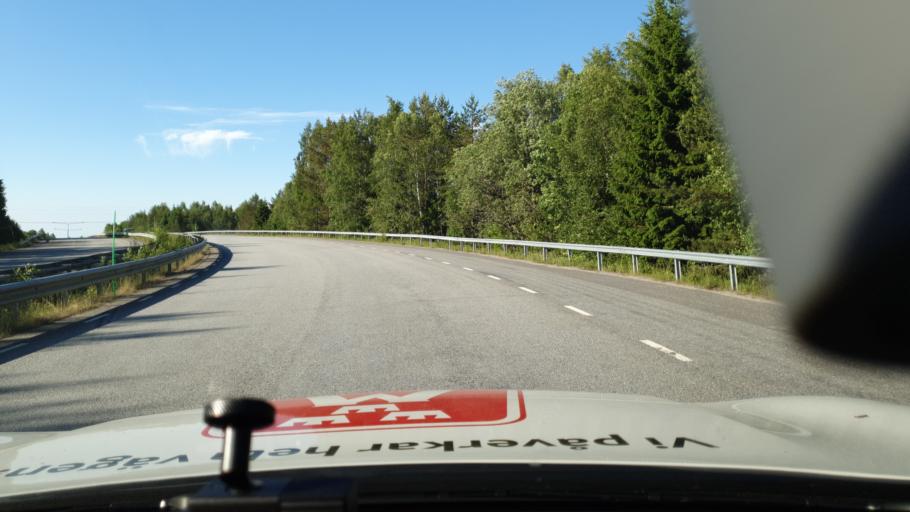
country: SE
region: Vaesterbotten
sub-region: Umea Kommun
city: Roback
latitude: 63.7882
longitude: 20.2021
